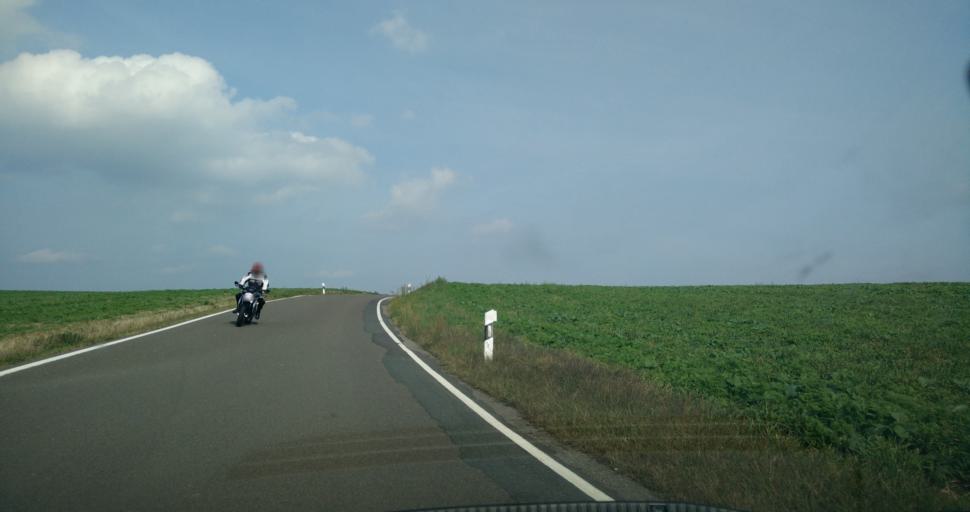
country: DE
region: Saxony
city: Colditz
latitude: 51.0900
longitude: 12.7948
